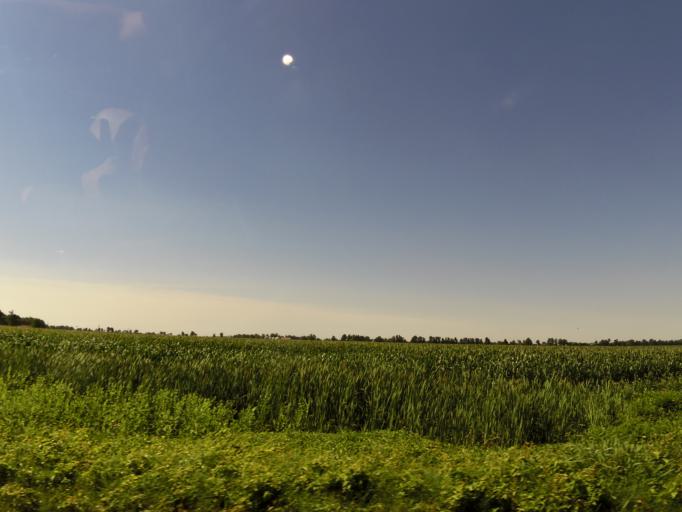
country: US
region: Arkansas
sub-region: Clay County
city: Piggott
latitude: 36.3820
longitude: -90.1615
